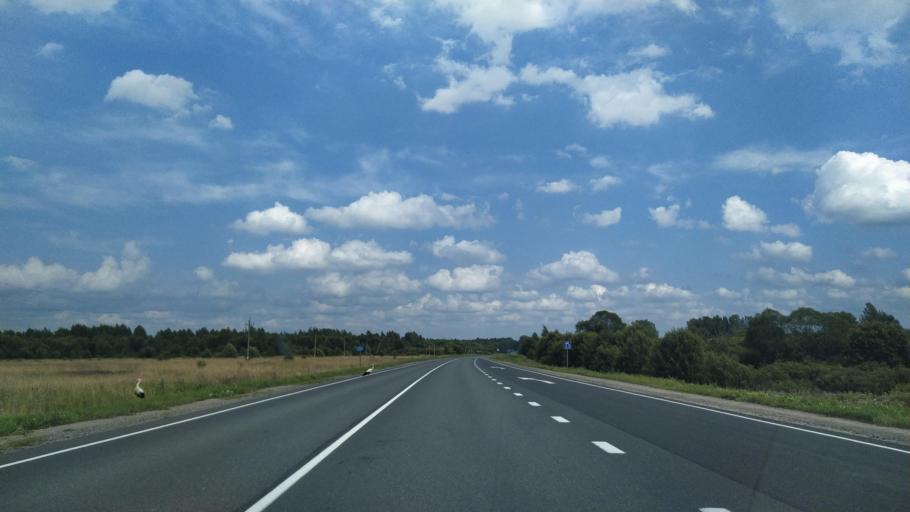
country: RU
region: Pskov
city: Dno
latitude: 57.9833
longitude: 29.7600
